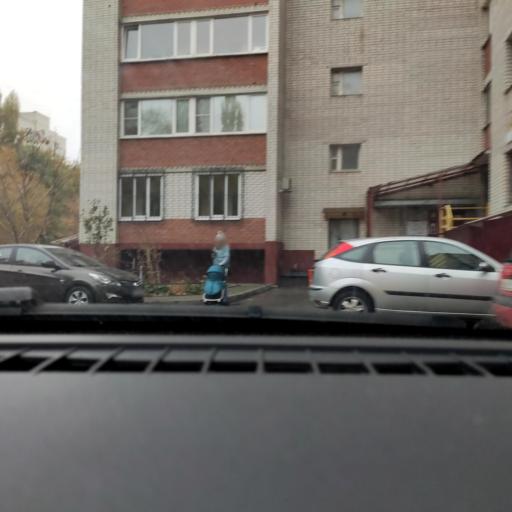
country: RU
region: Voronezj
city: Voronezh
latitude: 51.6407
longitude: 39.2319
